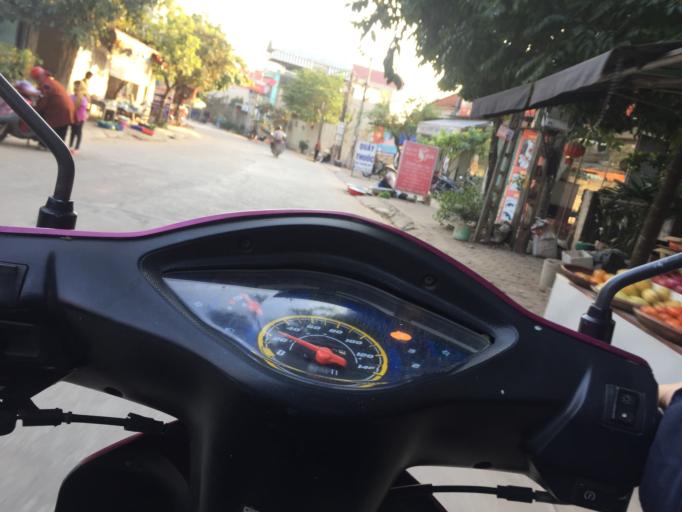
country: VN
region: Ha Noi
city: Chuc Son
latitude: 20.9153
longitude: 105.7140
